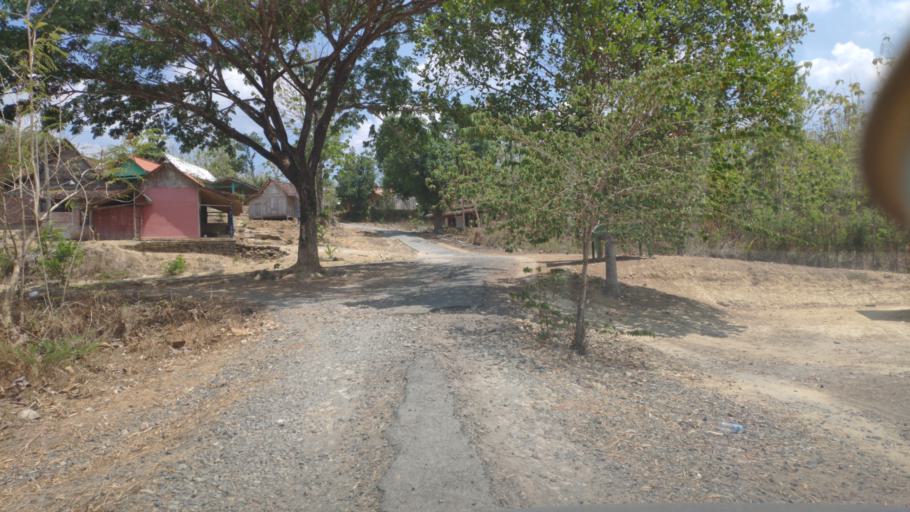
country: ID
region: Central Java
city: Prantaan
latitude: -6.9576
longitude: 111.5039
